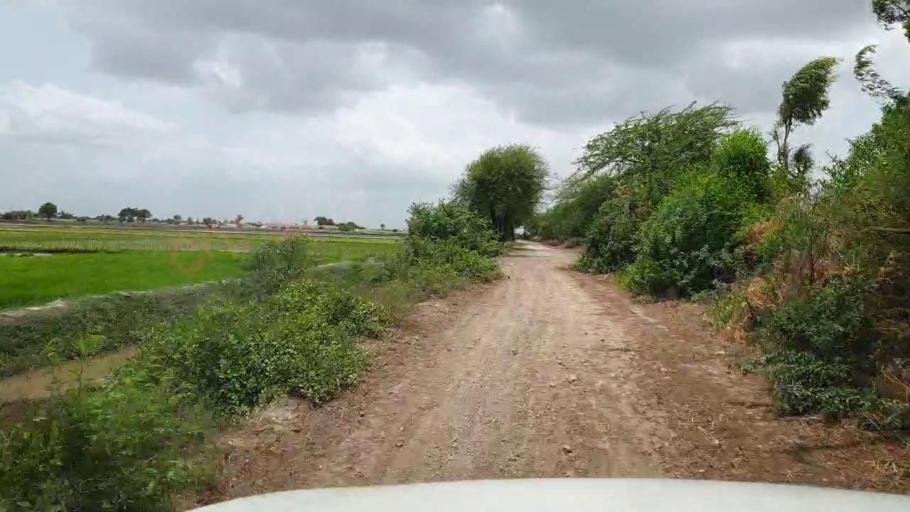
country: PK
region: Sindh
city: Kario
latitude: 24.7481
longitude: 68.4822
